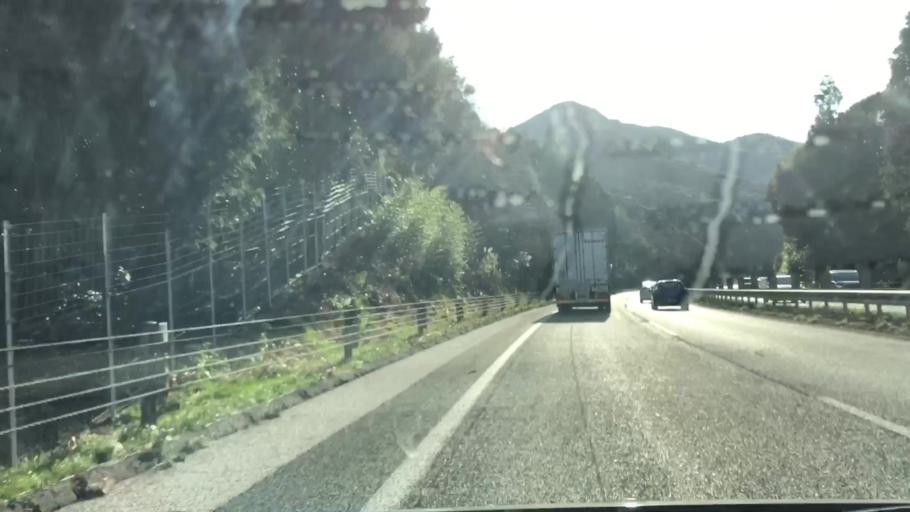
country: JP
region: Yamaguchi
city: Ogori-shimogo
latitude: 34.1754
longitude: 131.2680
